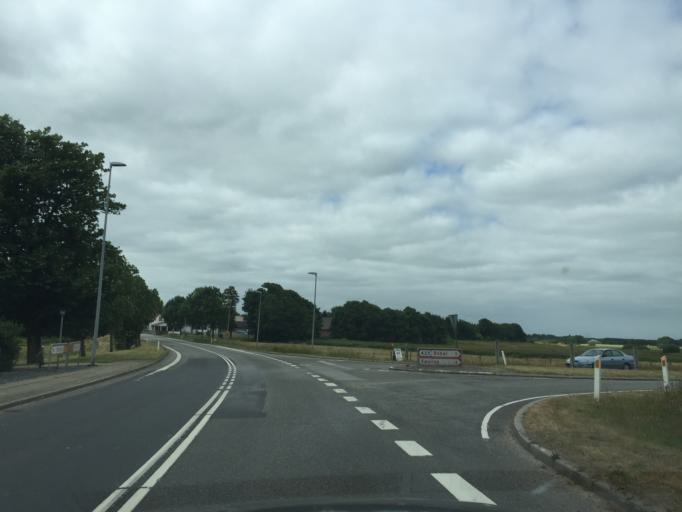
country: DK
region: South Denmark
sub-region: Vejen Kommune
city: Brorup
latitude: 55.4409
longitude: 8.9990
